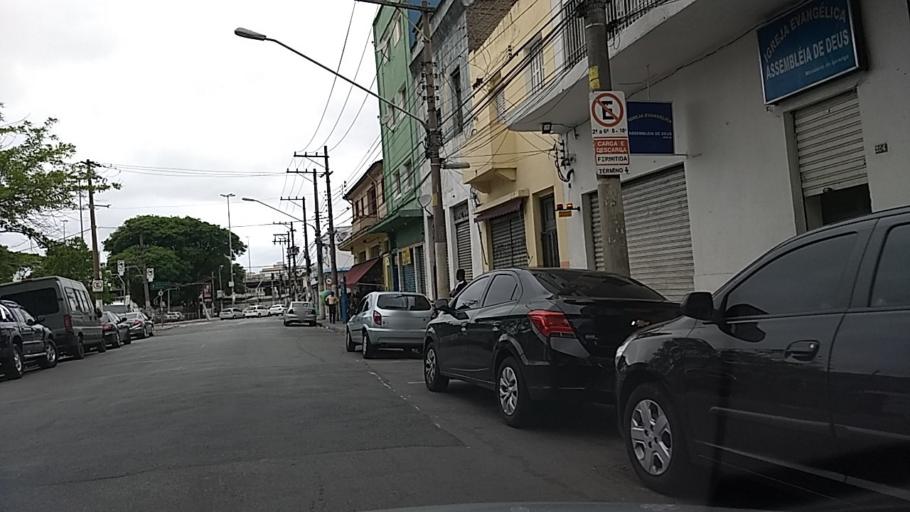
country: BR
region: Sao Paulo
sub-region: Sao Paulo
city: Sao Paulo
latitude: -23.5513
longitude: -46.6283
